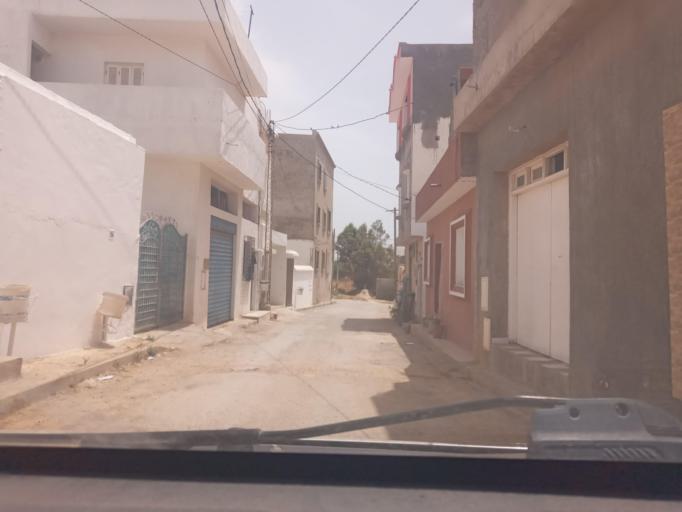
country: TN
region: Nabul
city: El Haouaria
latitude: 37.0525
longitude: 11.0148
